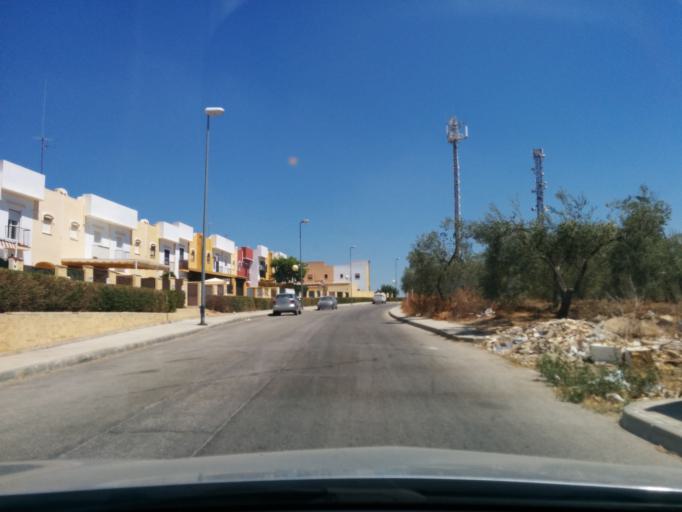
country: ES
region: Andalusia
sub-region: Provincia de Sevilla
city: Benacazon
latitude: 37.3564
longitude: -6.1942
